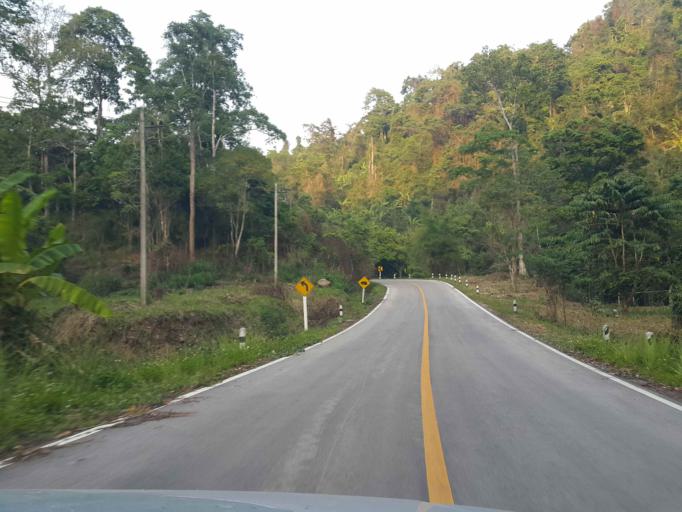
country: TH
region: Chiang Mai
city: Mae On
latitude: 18.9724
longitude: 99.3215
